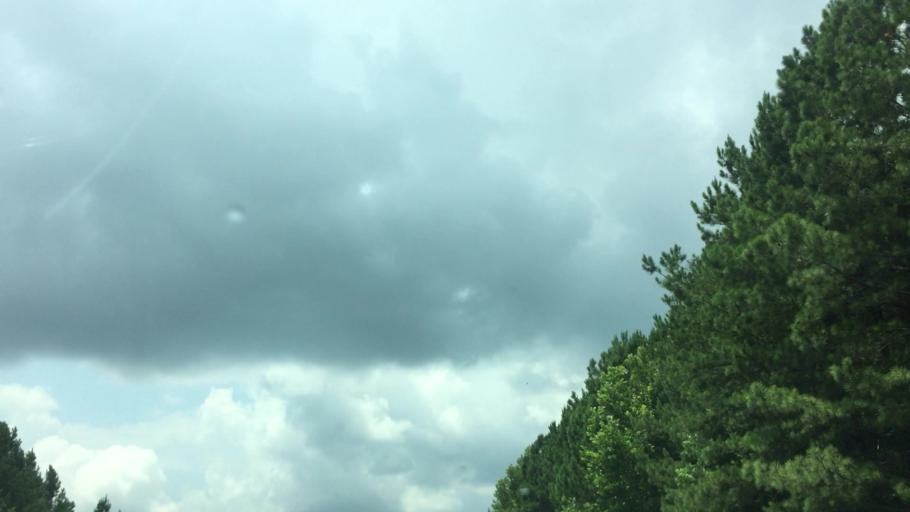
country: US
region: Georgia
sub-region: Fulton County
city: Fairburn
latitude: 33.6068
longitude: -84.6220
